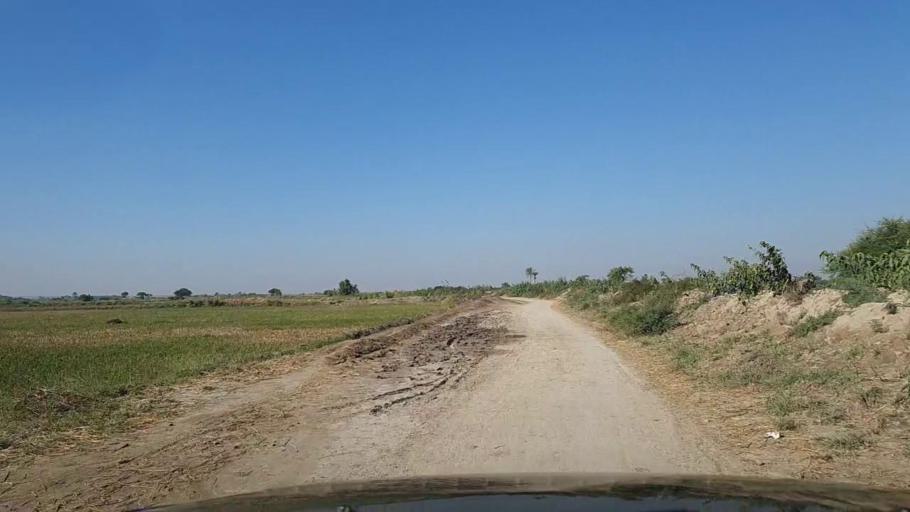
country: PK
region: Sindh
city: Thatta
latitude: 24.7184
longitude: 67.9261
